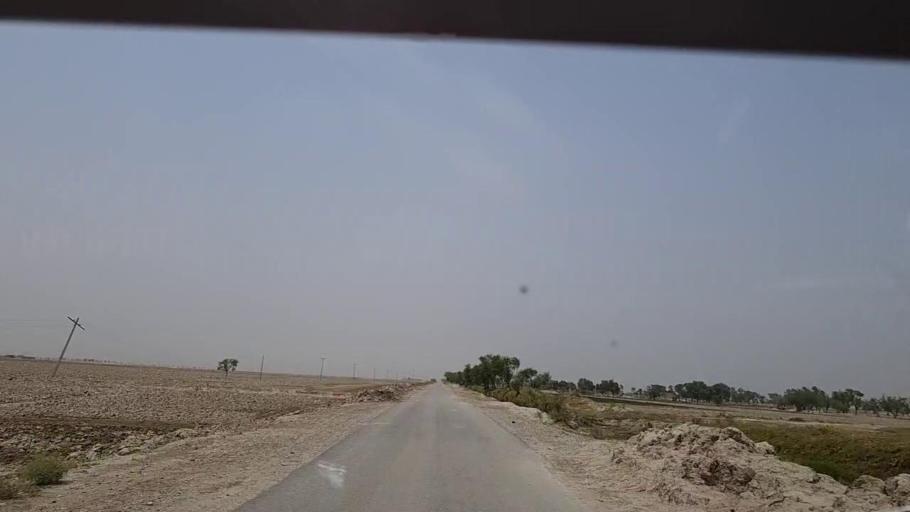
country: PK
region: Sindh
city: Khairpur Nathan Shah
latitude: 27.0254
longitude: 67.6208
